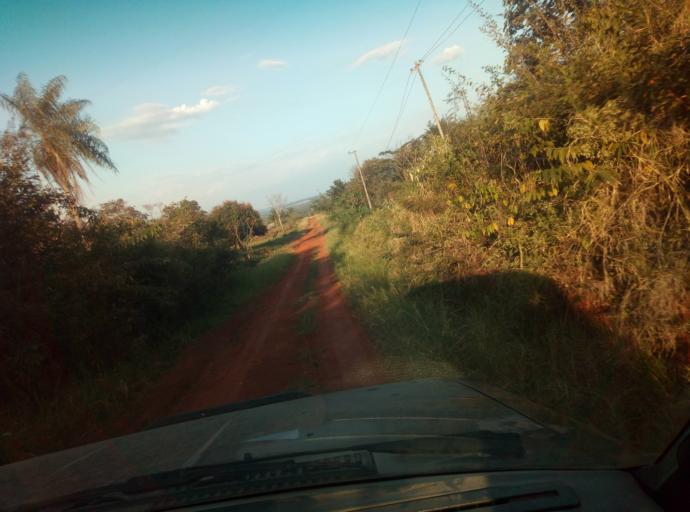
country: PY
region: Caaguazu
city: Doctor Cecilio Baez
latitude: -25.1524
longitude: -56.2448
